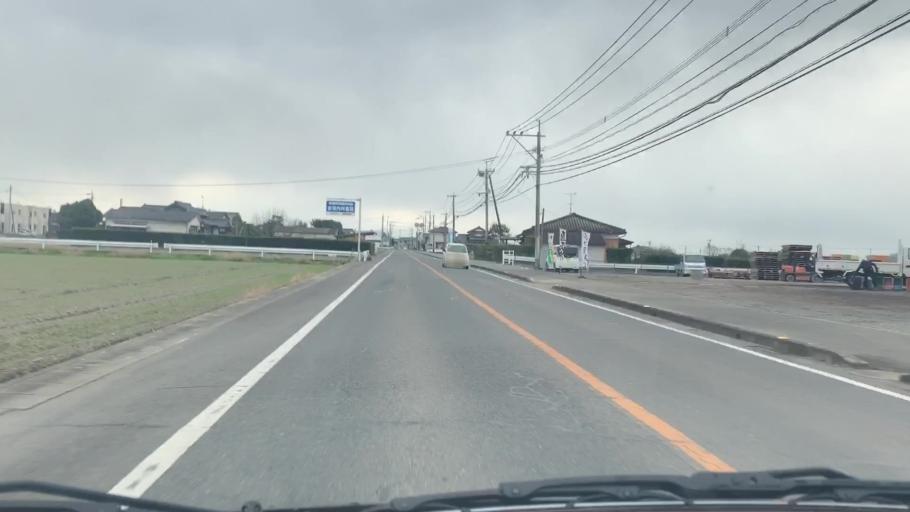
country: JP
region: Saga Prefecture
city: Kashima
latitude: 33.1825
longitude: 130.1831
